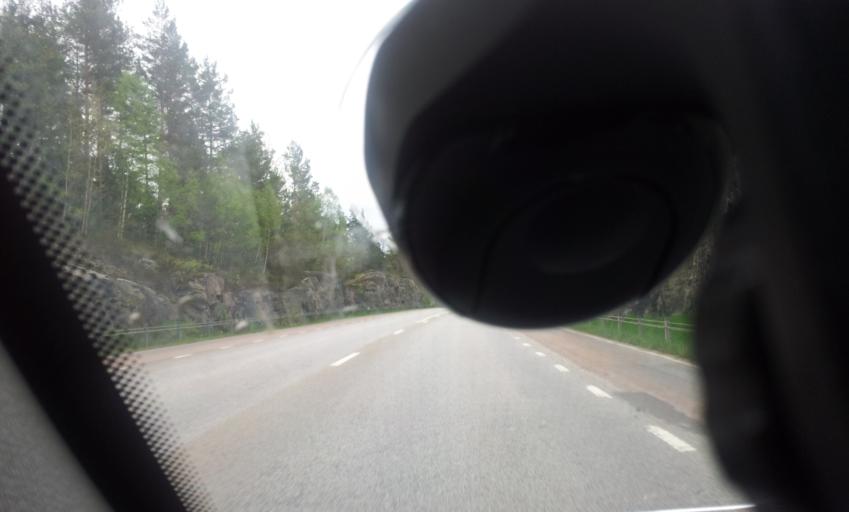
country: SE
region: Kalmar
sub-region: Vasterviks Kommun
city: Ankarsrum
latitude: 57.6481
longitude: 16.4430
